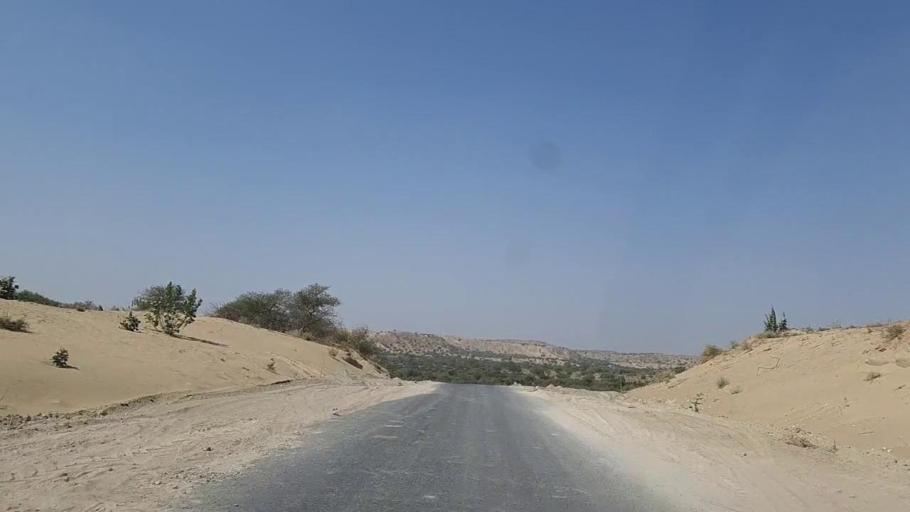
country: PK
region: Sindh
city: Diplo
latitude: 24.5871
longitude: 69.5335
